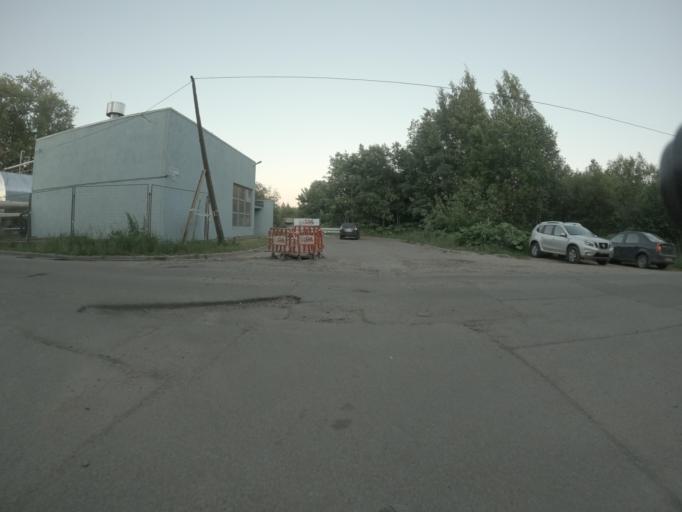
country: RU
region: St.-Petersburg
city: Krasnogvargeisky
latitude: 59.9840
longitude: 30.5202
